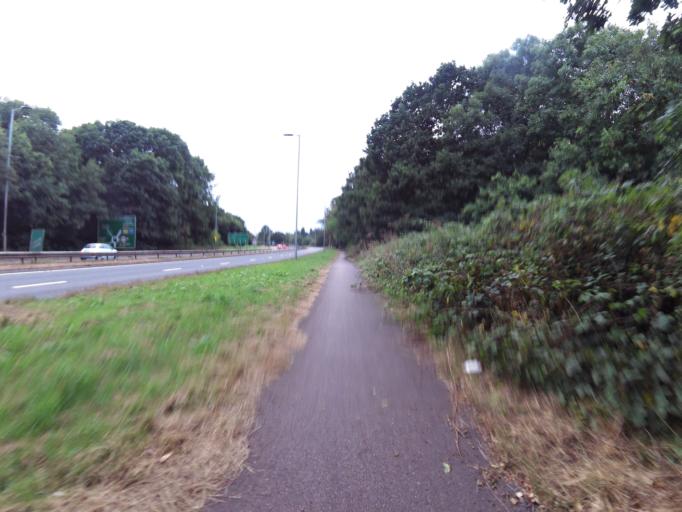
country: GB
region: England
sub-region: Hertfordshire
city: St Albans
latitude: 51.7315
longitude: -0.2977
